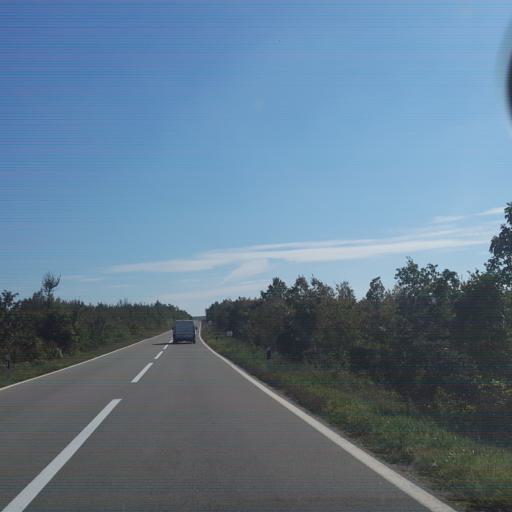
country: RS
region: Central Serbia
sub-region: Zajecarski Okrug
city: Knjazevac
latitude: 43.5035
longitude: 22.2149
